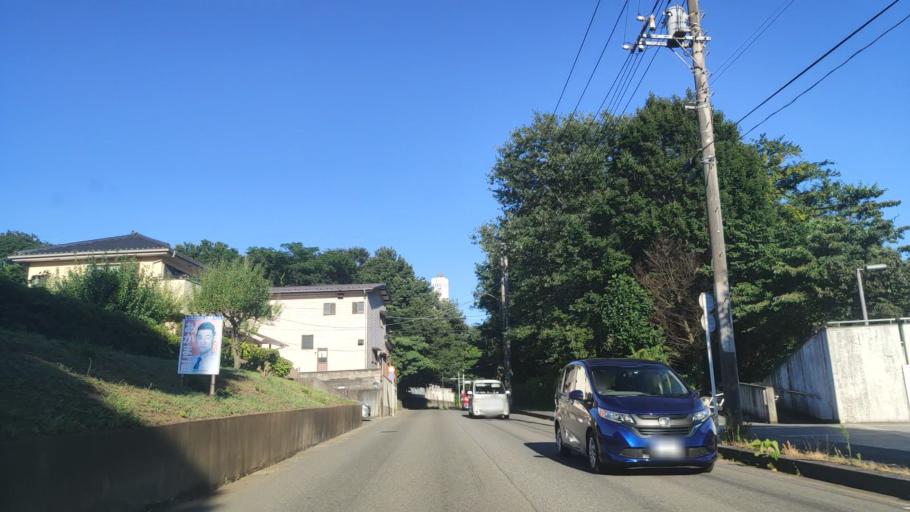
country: JP
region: Tokyo
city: Hachioji
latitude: 35.5854
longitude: 139.3288
